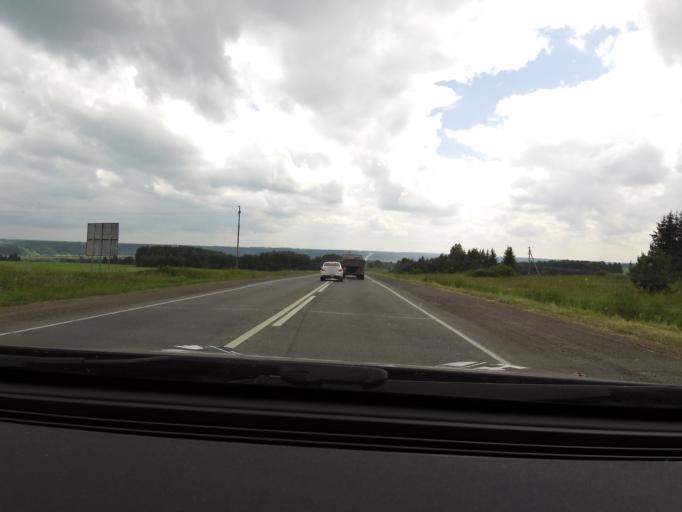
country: RU
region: Perm
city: Kungur
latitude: 57.3977
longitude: 56.8978
